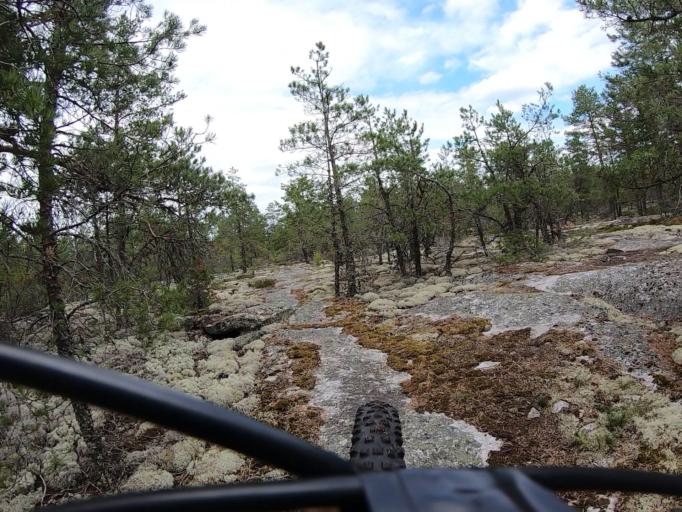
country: FI
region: Varsinais-Suomi
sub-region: Vakka-Suomi
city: Uusikaupunki
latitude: 60.8380
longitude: 21.3936
